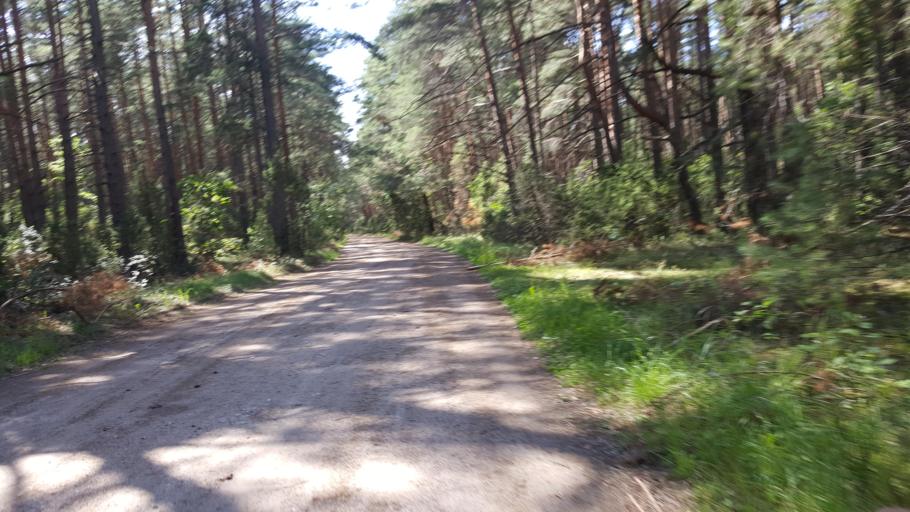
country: BY
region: Brest
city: Zhabinka
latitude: 52.4601
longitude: 24.1345
